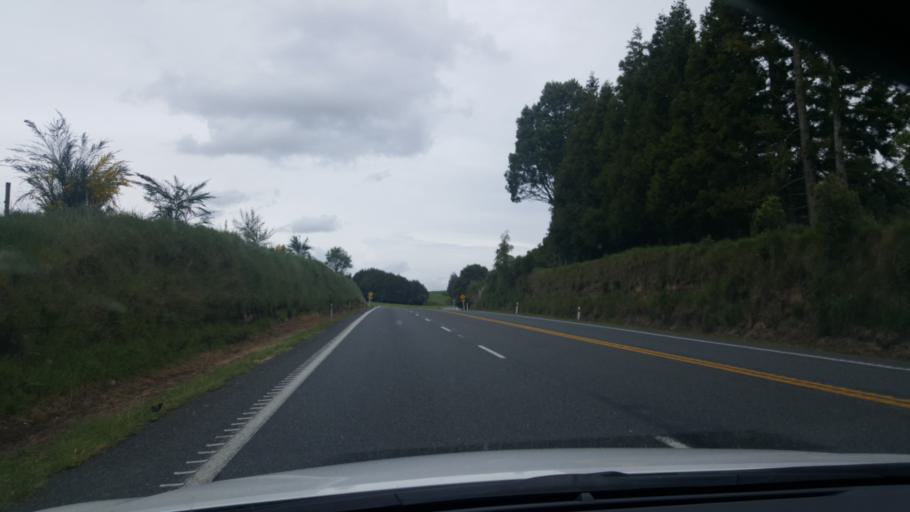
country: NZ
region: Bay of Plenty
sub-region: Rotorua District
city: Rotorua
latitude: -38.2469
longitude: 176.3146
